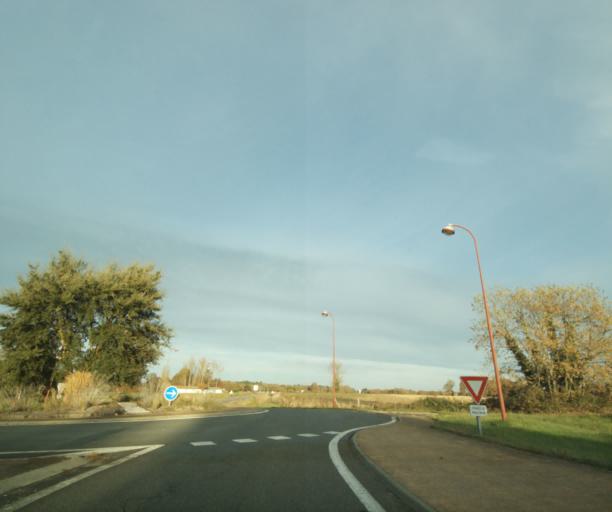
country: FR
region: Aquitaine
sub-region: Departement des Landes
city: Gabarret
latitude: 44.1063
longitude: -0.1029
